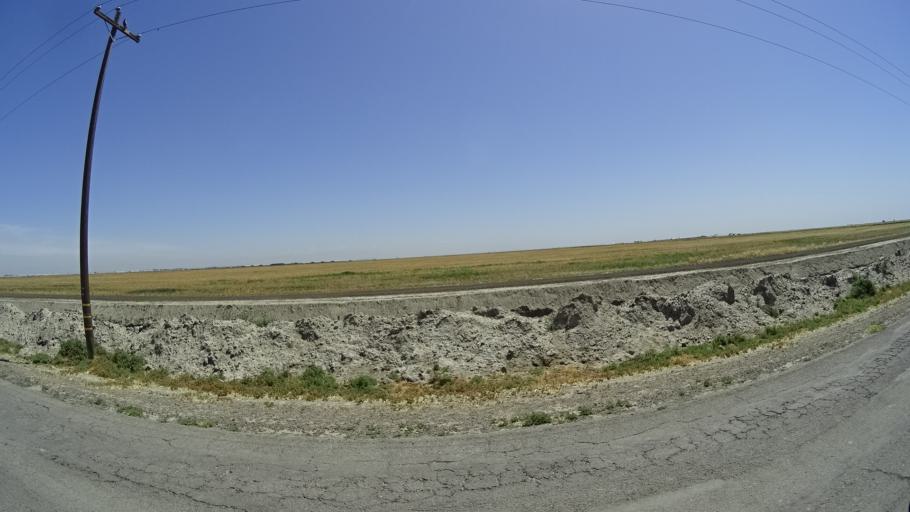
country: US
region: California
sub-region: Kings County
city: Stratford
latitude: 36.1773
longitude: -119.7175
